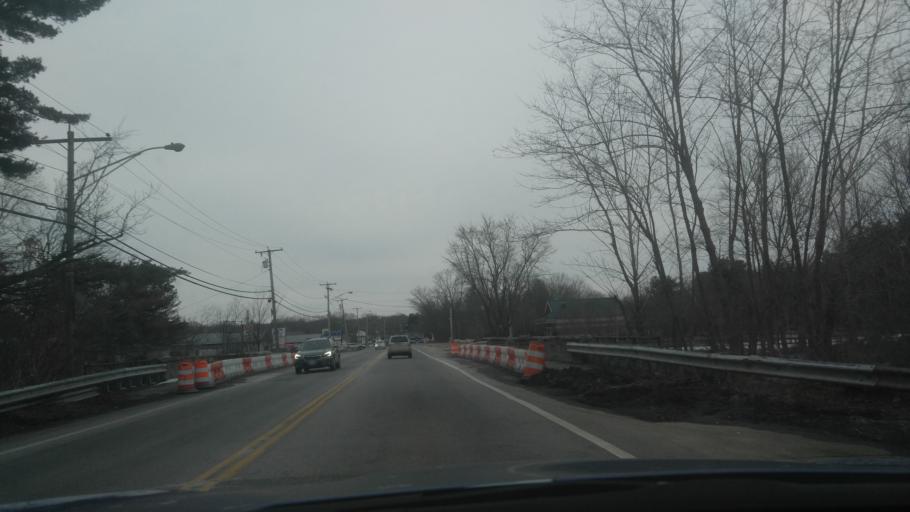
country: US
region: Rhode Island
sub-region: Kent County
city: West Warwick
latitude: 41.6856
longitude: -71.5608
